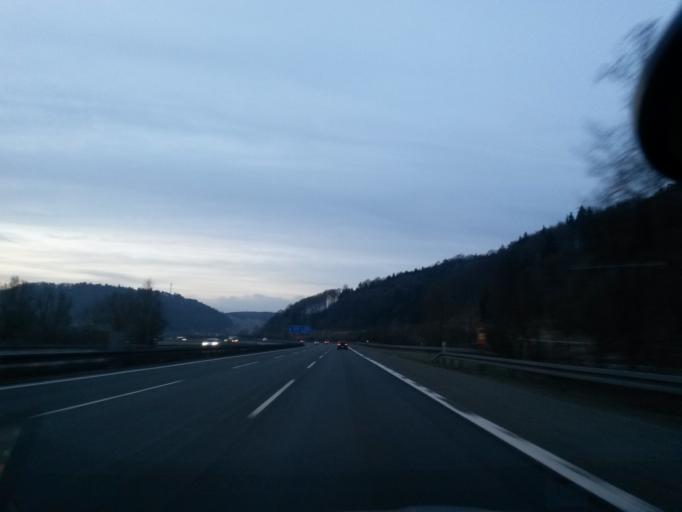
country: DE
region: Bavaria
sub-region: Regierungsbezirk Mittelfranken
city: Greding
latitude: 49.0065
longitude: 11.3551
